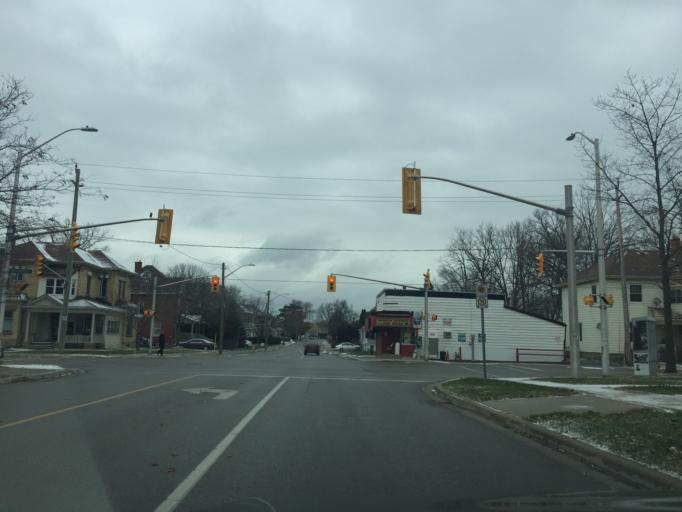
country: CA
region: Ontario
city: St. Thomas
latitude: 42.7750
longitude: -81.1985
